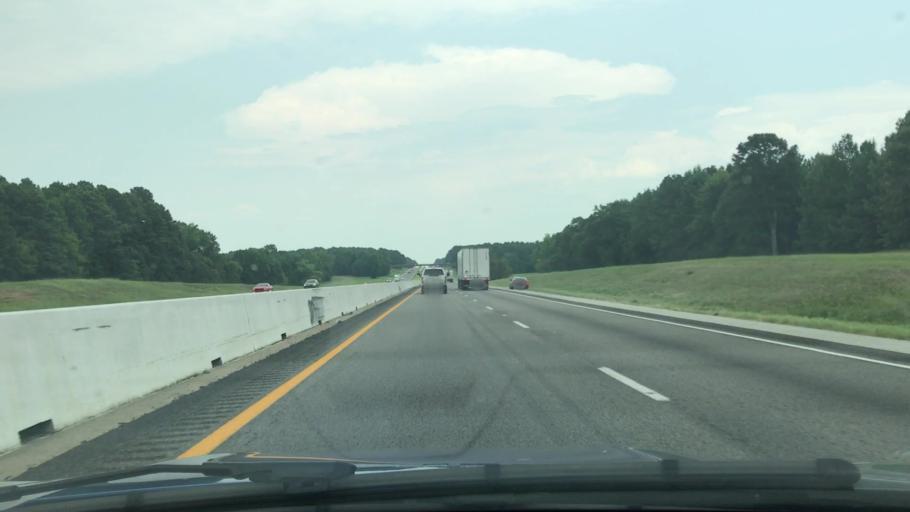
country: US
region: Texas
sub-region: Gregg County
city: Liberty City
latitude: 32.4373
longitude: -95.0196
